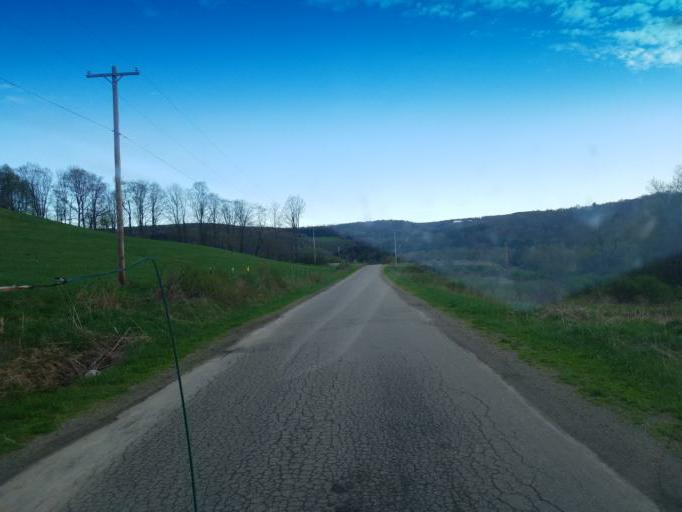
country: US
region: New York
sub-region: Allegany County
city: Andover
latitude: 42.0317
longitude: -77.7606
